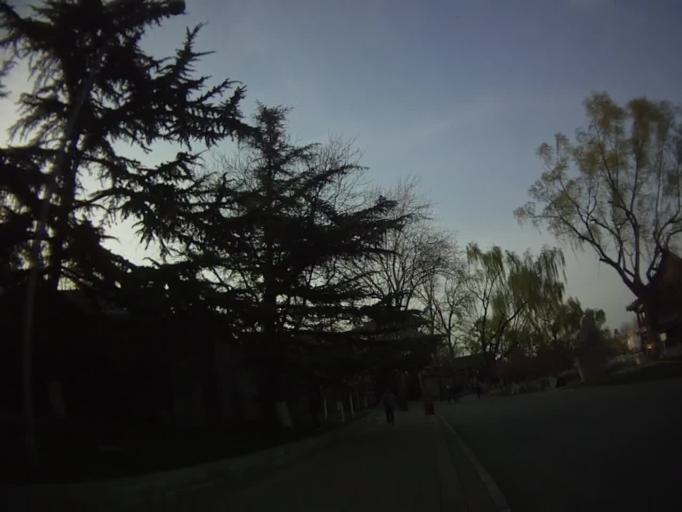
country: CN
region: Beijing
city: Longtan
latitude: 39.8757
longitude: 116.4328
